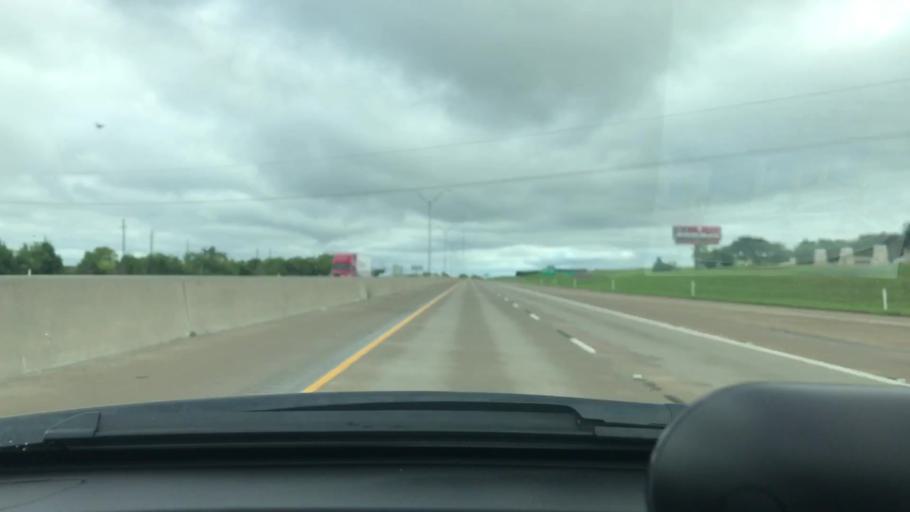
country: US
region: Texas
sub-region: Grayson County
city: Howe
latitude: 33.5140
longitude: -96.6163
